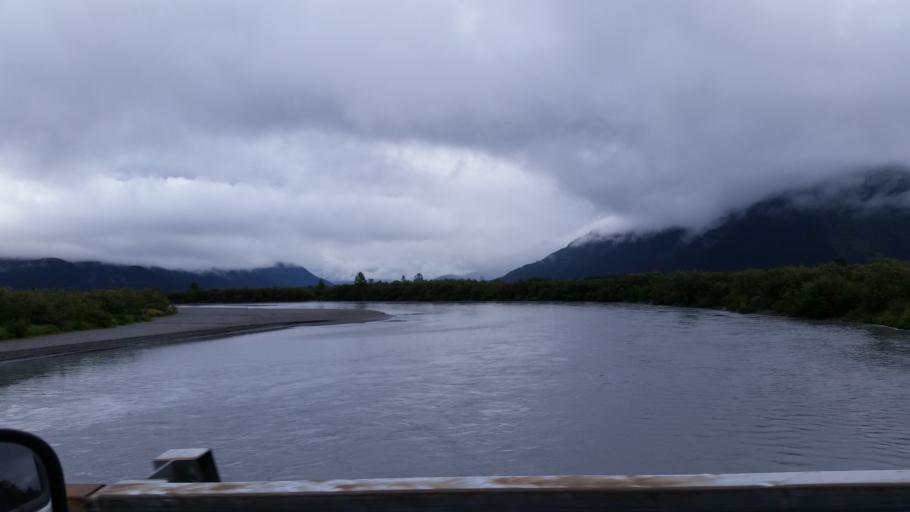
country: US
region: Alaska
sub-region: Anchorage Municipality
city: Girdwood
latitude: 60.8199
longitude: -149.0006
